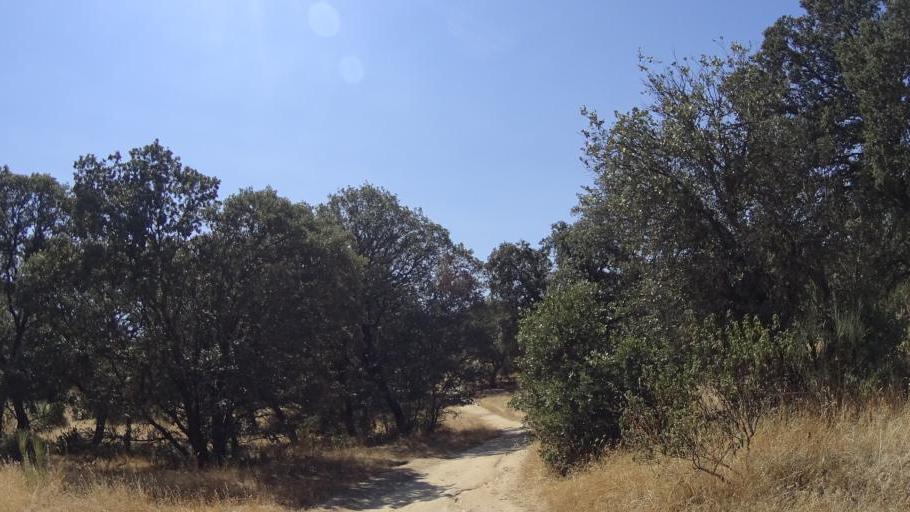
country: ES
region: Madrid
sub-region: Provincia de Madrid
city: Boadilla del Monte
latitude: 40.4388
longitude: -3.8730
